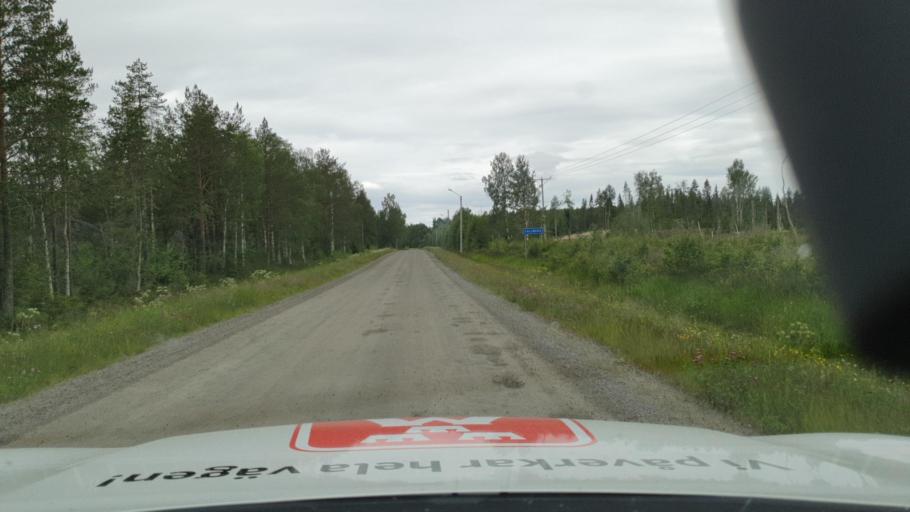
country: SE
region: Vaesterbotten
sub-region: Nordmalings Kommun
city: Nordmaling
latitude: 63.7760
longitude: 19.4017
